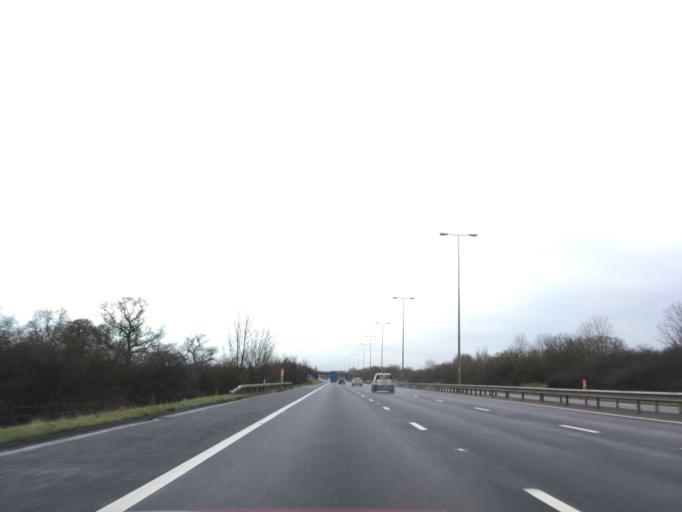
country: GB
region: England
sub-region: Worcestershire
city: Kempsey
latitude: 52.1344
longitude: -2.1994
